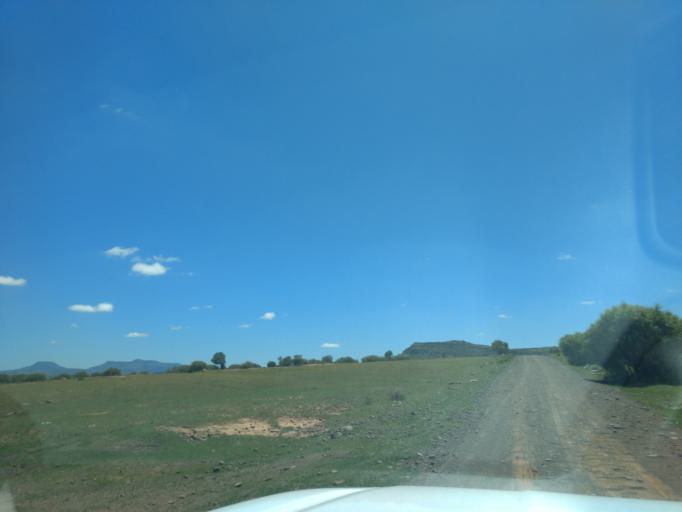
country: LS
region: Maseru
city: Maseru
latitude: -29.4563
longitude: 27.3680
